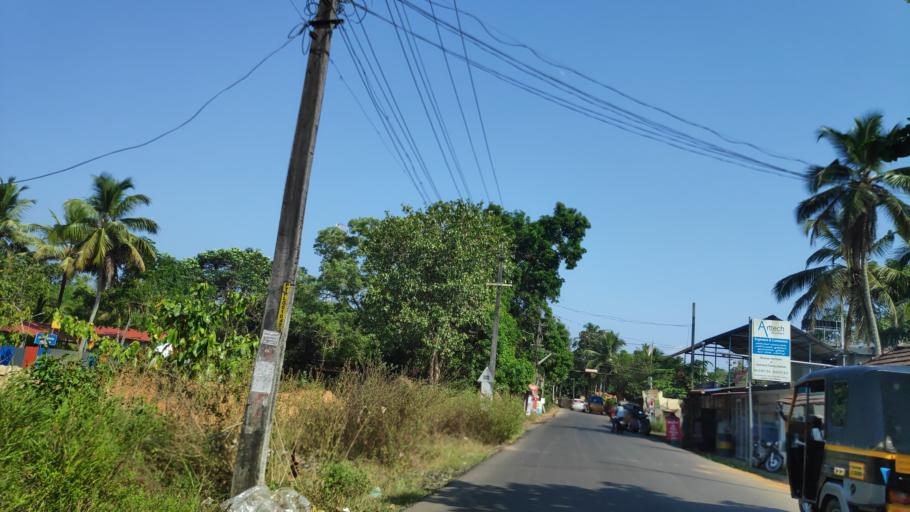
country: IN
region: Kerala
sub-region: Alappuzha
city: Alleppey
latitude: 9.5703
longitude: 76.3172
